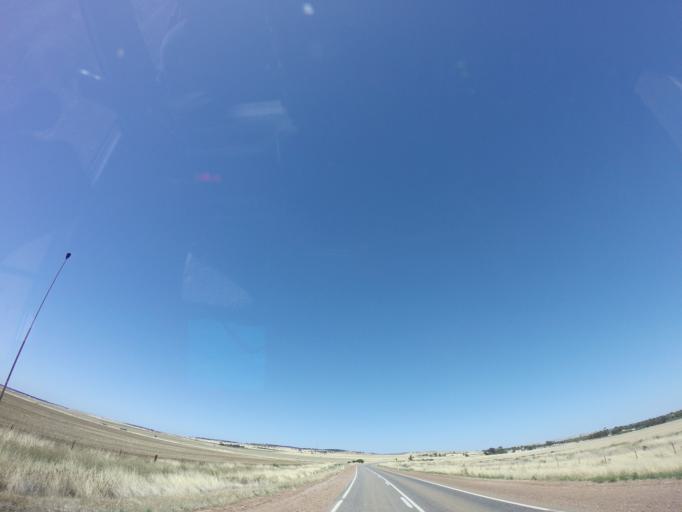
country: AU
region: South Australia
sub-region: Peterborough
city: Peterborough
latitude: -32.9687
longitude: 138.8109
